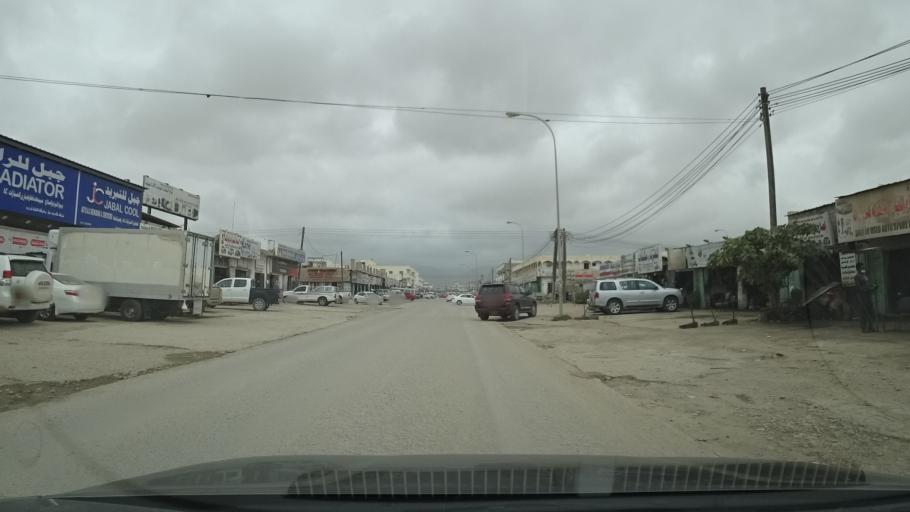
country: OM
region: Zufar
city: Salalah
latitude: 17.0180
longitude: 54.0533
